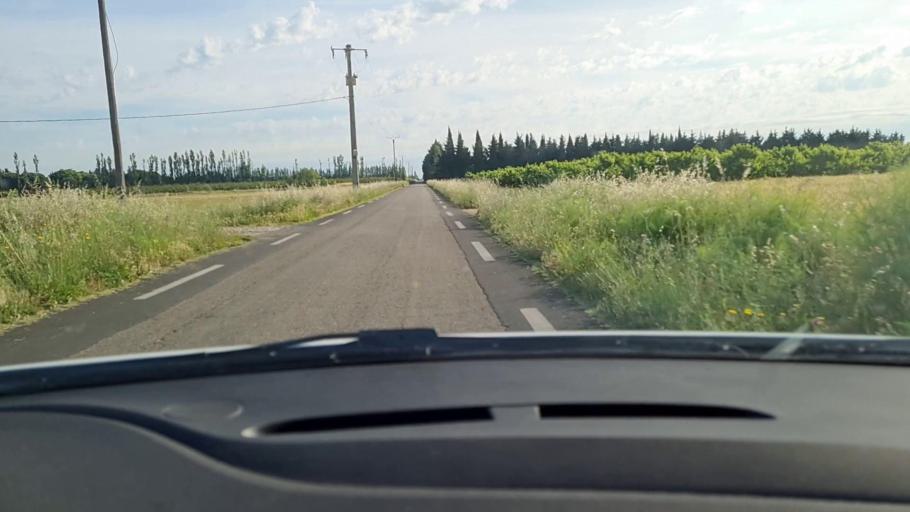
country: FR
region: Languedoc-Roussillon
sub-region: Departement du Gard
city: Jonquieres-Saint-Vincent
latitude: 43.7996
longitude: 4.5365
